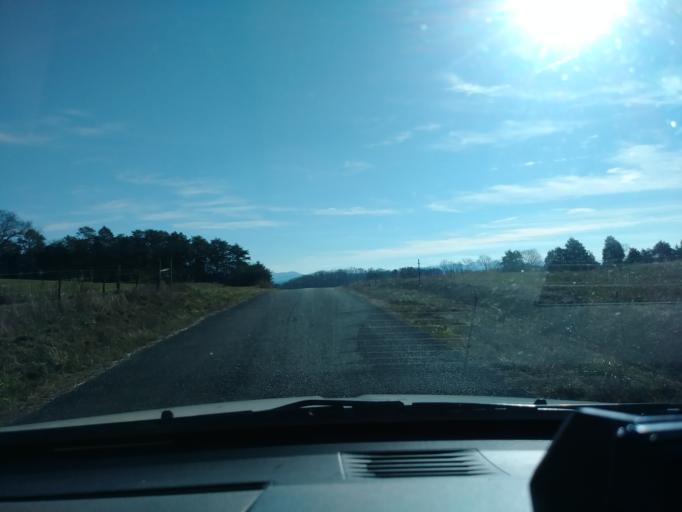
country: US
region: Tennessee
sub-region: Greene County
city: Greeneville
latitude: 36.0828
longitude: -82.8966
